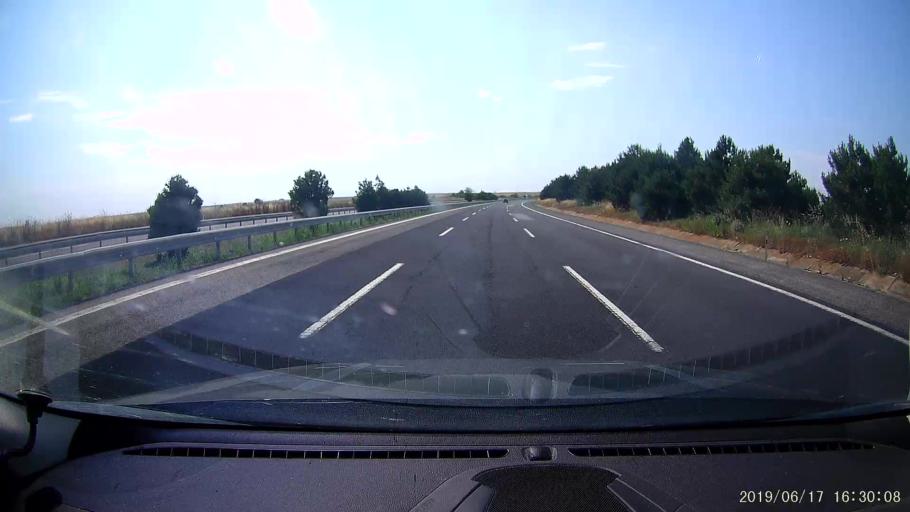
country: TR
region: Tekirdag
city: Beyazkoy
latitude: 41.3424
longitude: 27.6624
